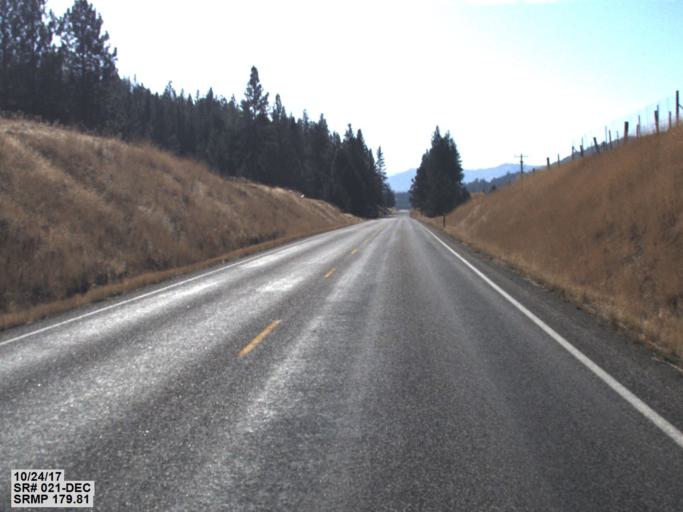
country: CA
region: British Columbia
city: Grand Forks
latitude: 48.8652
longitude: -118.6055
